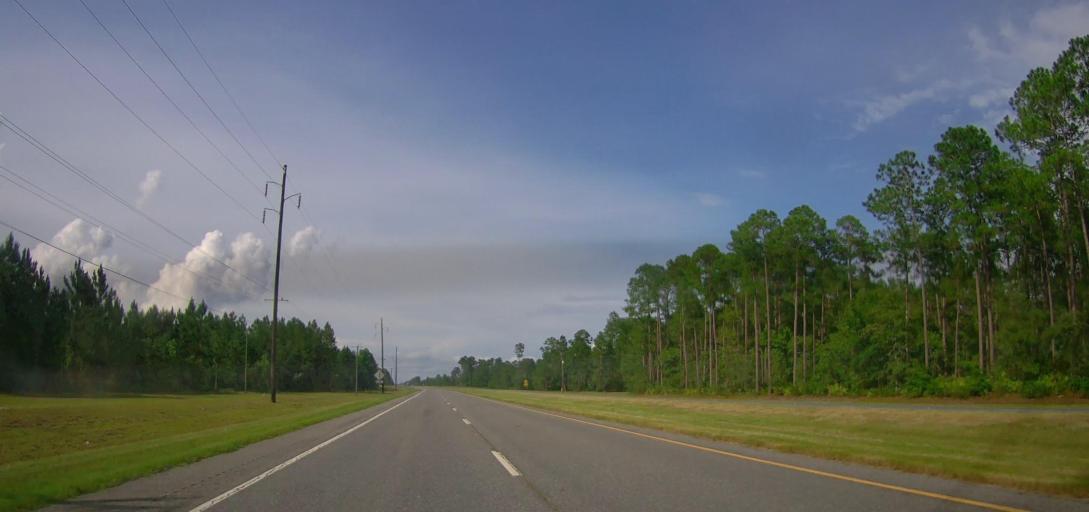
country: US
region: Georgia
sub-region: Wayne County
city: Jesup
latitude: 31.5266
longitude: -81.9866
